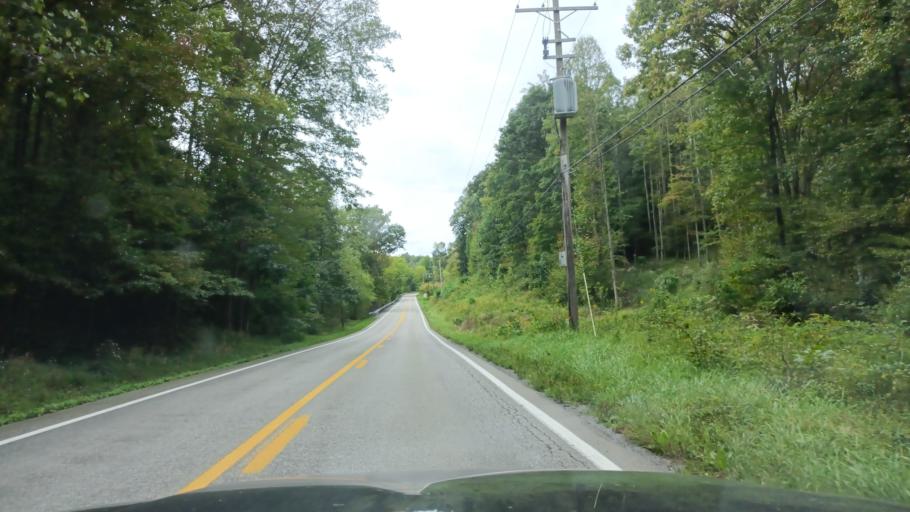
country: US
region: West Virginia
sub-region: Taylor County
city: Grafton
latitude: 39.3202
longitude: -80.1215
